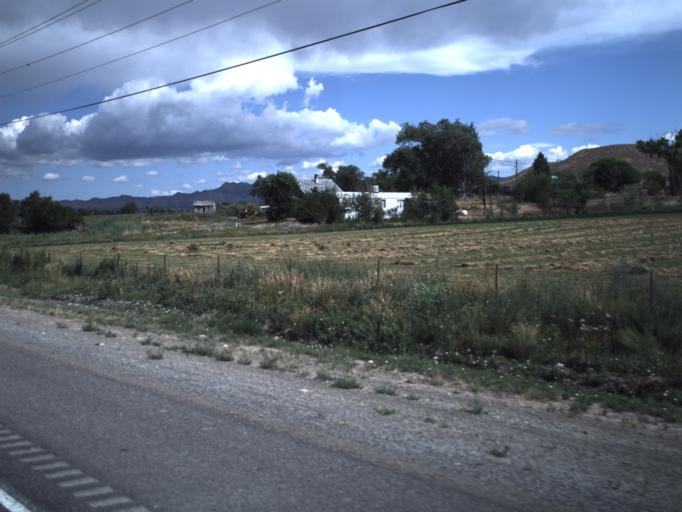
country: US
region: Utah
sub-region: Carbon County
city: Wellington
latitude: 39.5549
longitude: -110.7590
